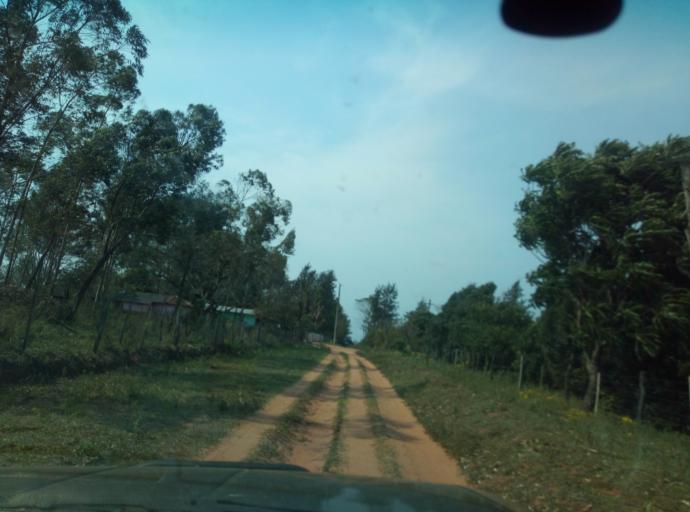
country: PY
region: Caaguazu
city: San Joaquin
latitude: -25.1461
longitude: -56.0985
